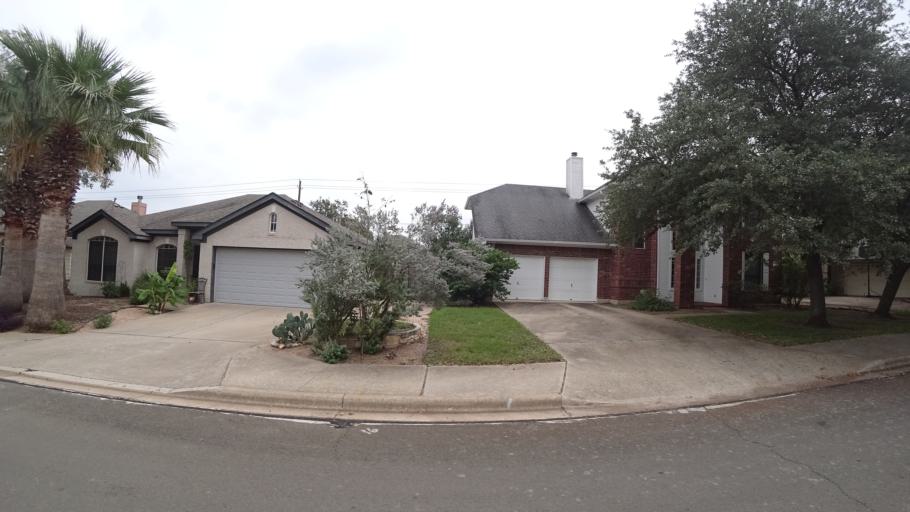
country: US
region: Texas
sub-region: Travis County
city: Shady Hollow
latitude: 30.2089
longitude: -97.8851
